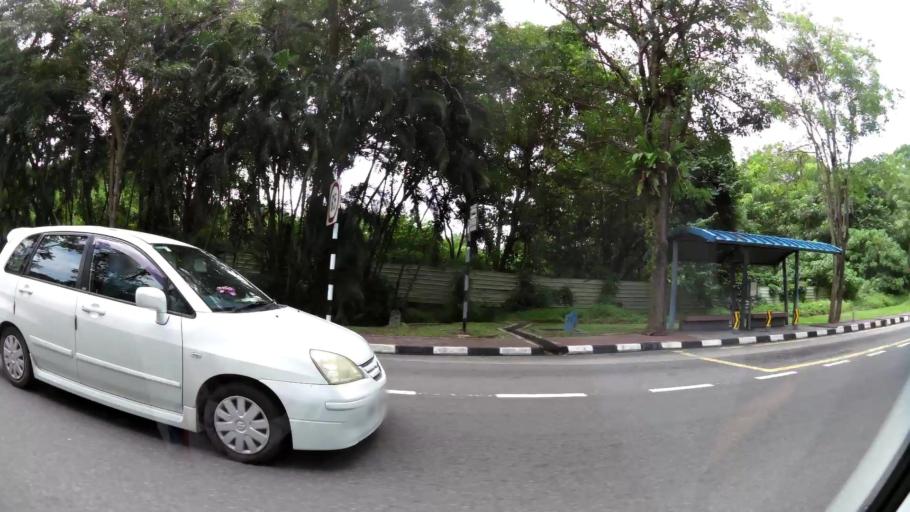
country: BN
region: Brunei and Muara
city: Bandar Seri Begawan
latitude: 4.9094
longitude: 114.9149
